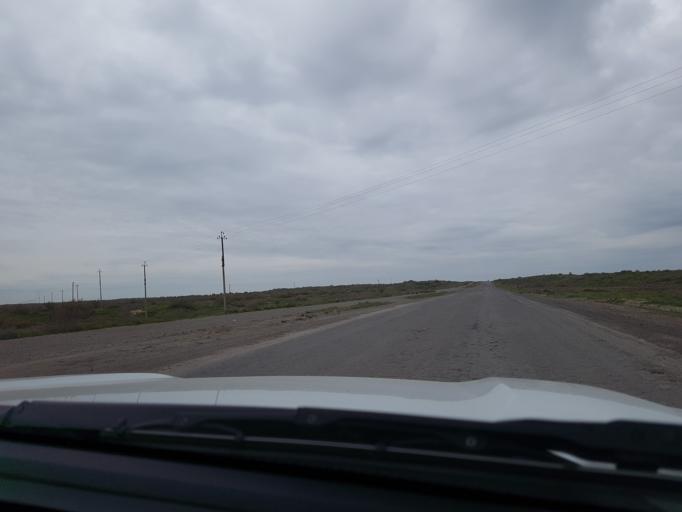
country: TM
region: Mary
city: Bayramaly
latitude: 37.9182
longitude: 62.6229
